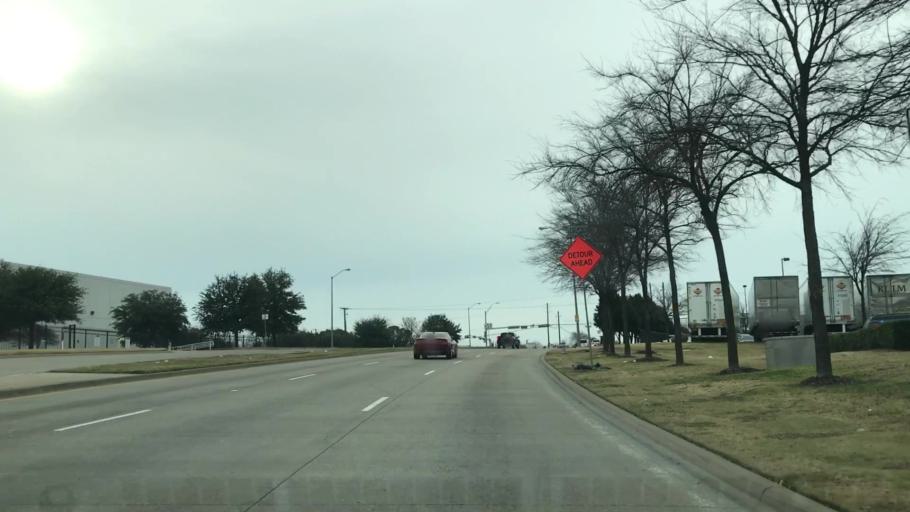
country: US
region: Texas
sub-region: Dallas County
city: Cockrell Hill
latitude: 32.7514
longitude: -96.8916
